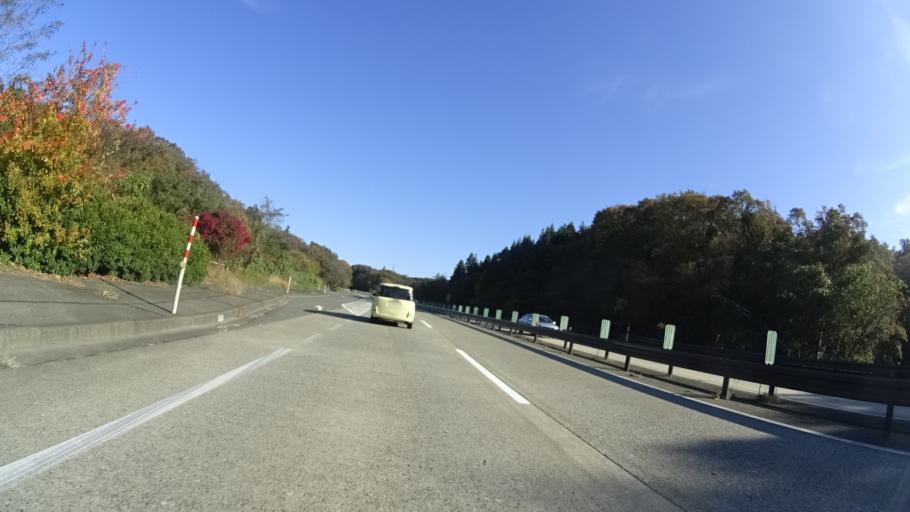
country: JP
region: Ishikawa
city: Komatsu
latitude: 36.3456
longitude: 136.4491
